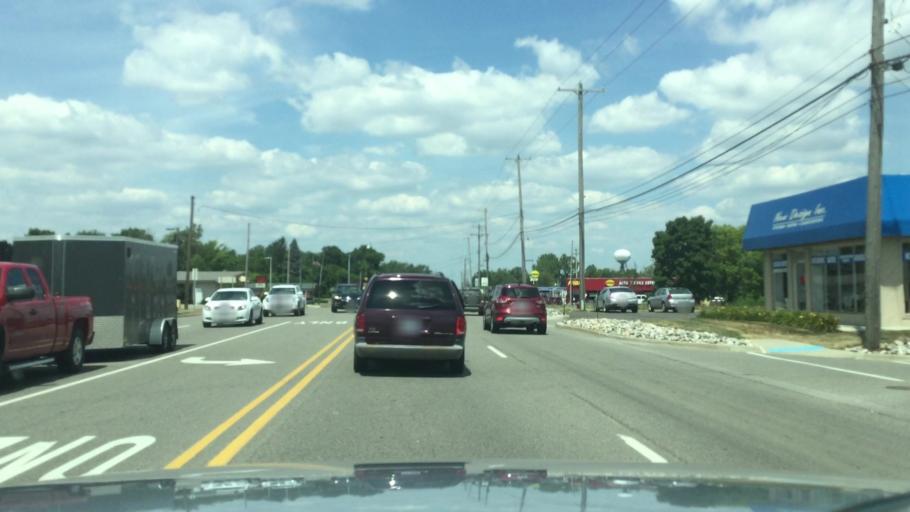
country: US
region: Michigan
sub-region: Genesee County
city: Grand Blanc
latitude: 42.9450
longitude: -83.6510
